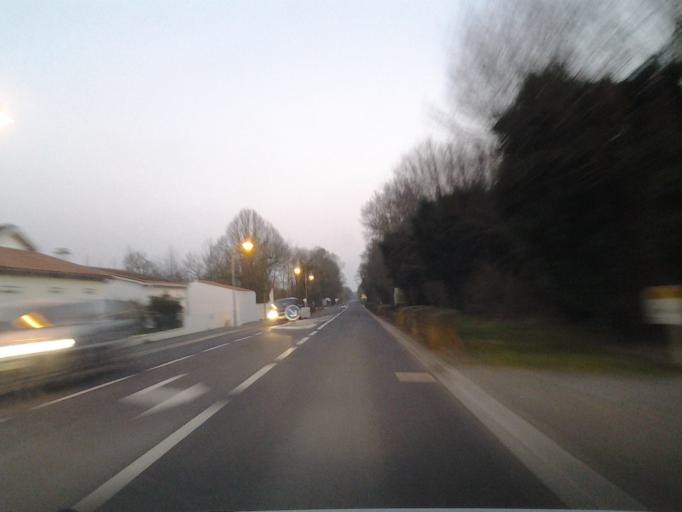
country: FR
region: Pays de la Loire
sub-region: Departement de la Vendee
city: Saint-Gervais
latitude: 46.8999
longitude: -1.9884
